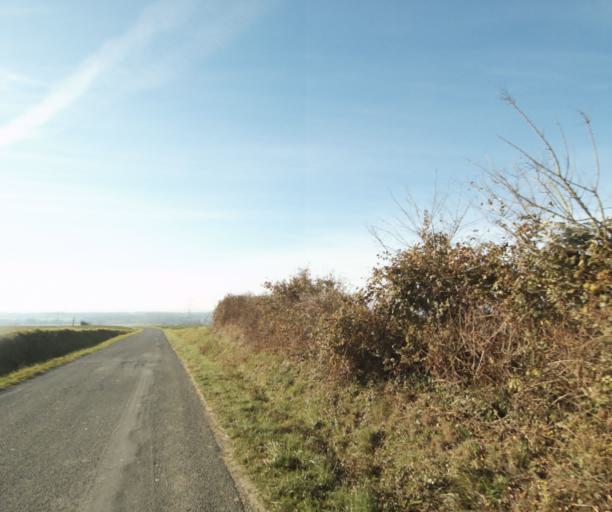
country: FR
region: Poitou-Charentes
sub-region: Departement de la Charente-Maritime
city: Chaniers
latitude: 45.7333
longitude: -0.5763
